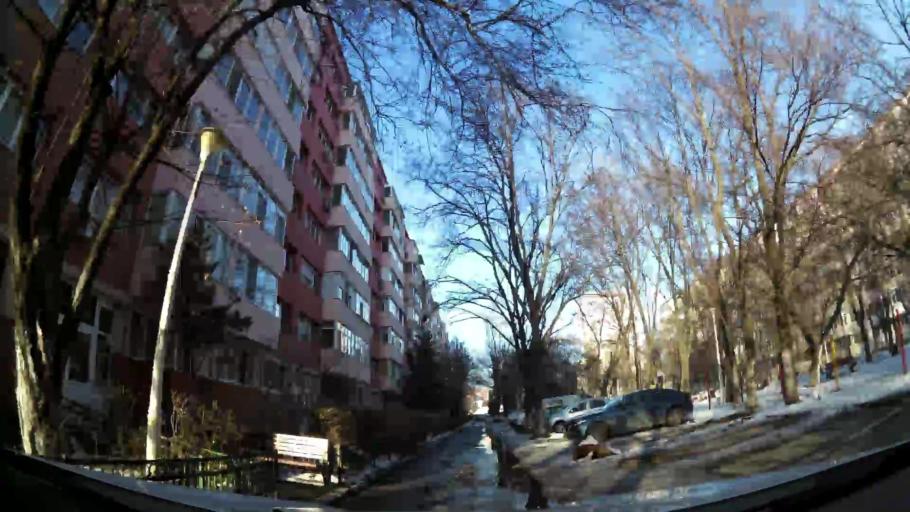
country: RO
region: Bucuresti
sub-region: Municipiul Bucuresti
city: Bucuresti
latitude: 44.3885
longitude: 26.0904
